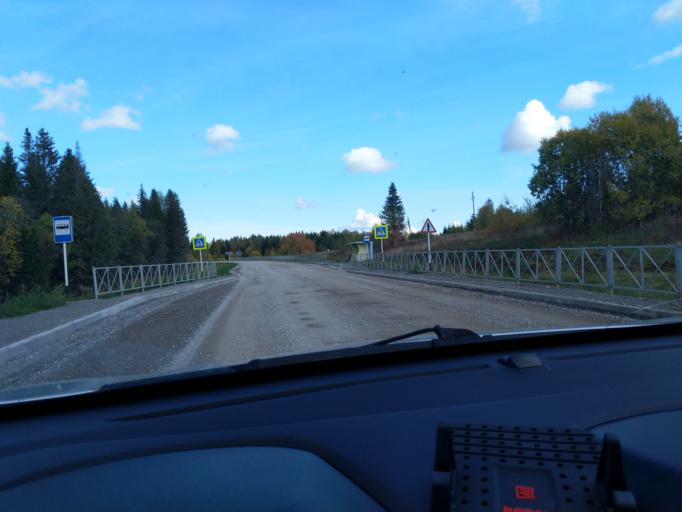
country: RU
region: Perm
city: Usol'ye
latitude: 59.4629
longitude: 56.3660
